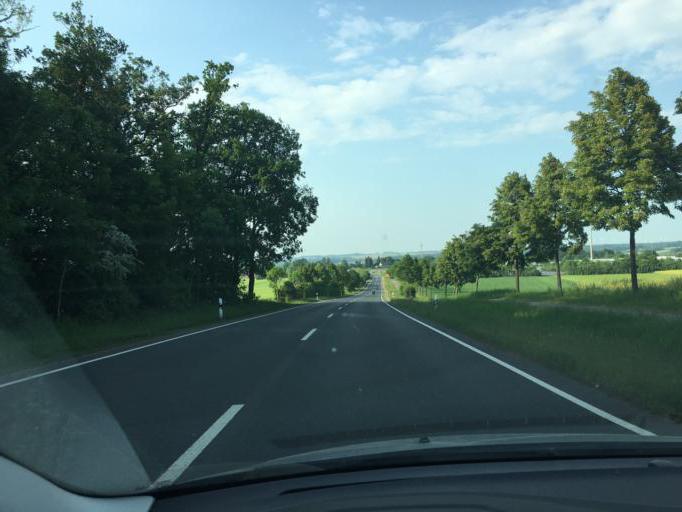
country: DE
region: Saxony
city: Grossbothen
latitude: 51.1740
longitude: 12.7596
